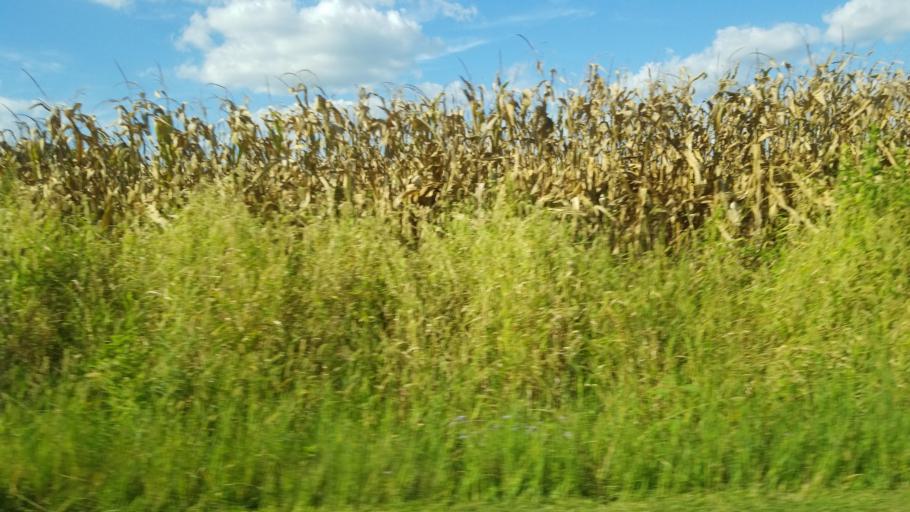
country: US
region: Illinois
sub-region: Saline County
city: Harrisburg
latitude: 37.8273
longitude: -88.5475
